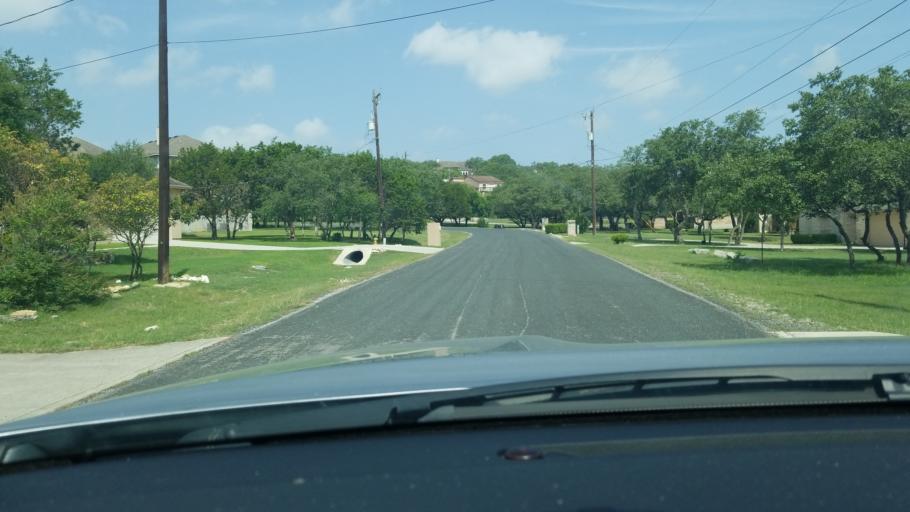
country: US
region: Texas
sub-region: Bexar County
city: Timberwood Park
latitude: 29.6864
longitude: -98.4887
